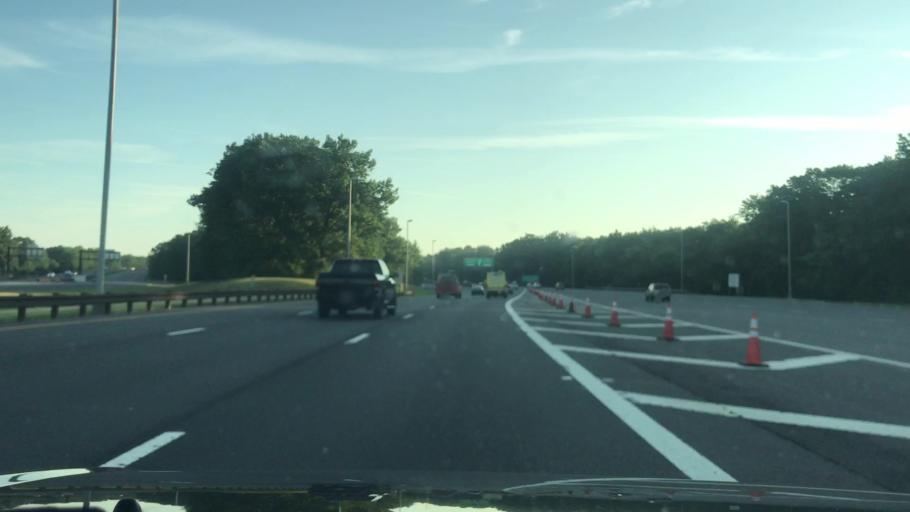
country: US
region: New Jersey
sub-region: Monmouth County
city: Eatontown
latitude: 40.2522
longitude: -74.0814
